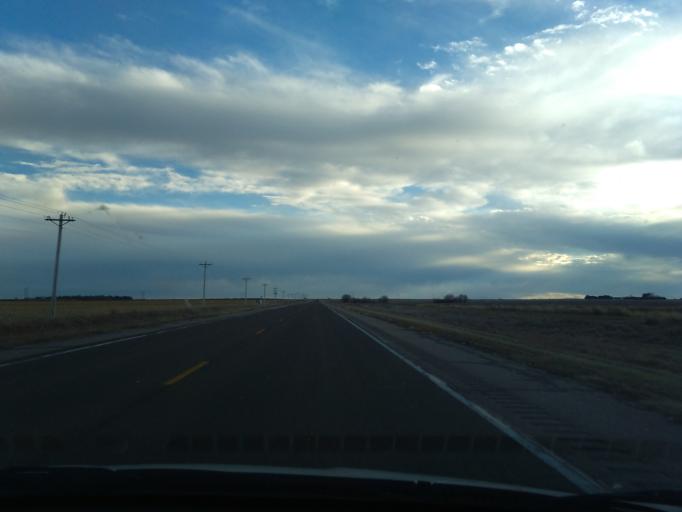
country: US
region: Nebraska
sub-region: Phelps County
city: Holdrege
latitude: 40.3934
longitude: -99.3700
